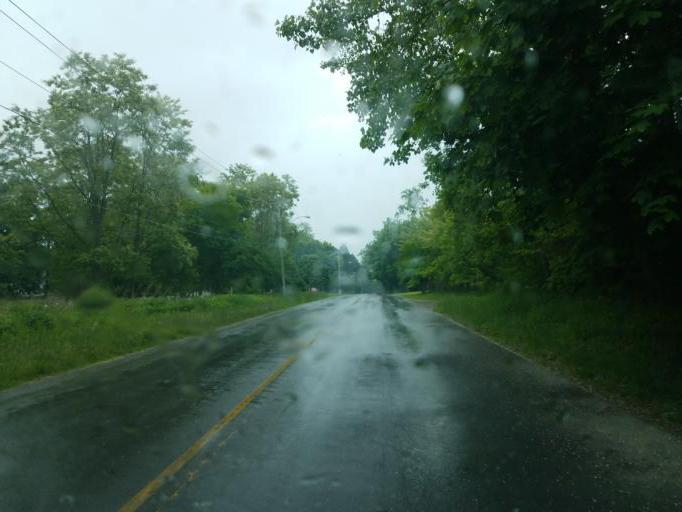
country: US
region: New York
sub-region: Herkimer County
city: Herkimer
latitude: 43.0284
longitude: -75.0017
